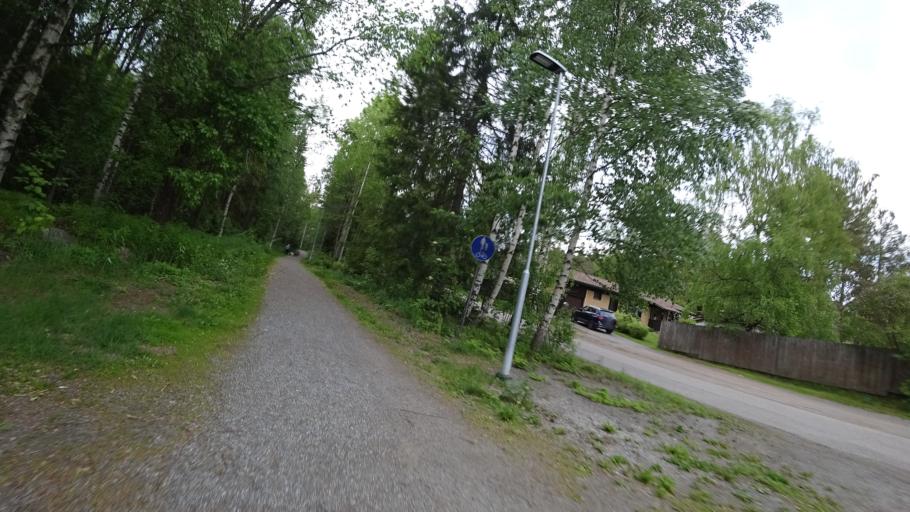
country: FI
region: Pirkanmaa
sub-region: Tampere
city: Yloejaervi
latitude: 61.5189
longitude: 23.6069
